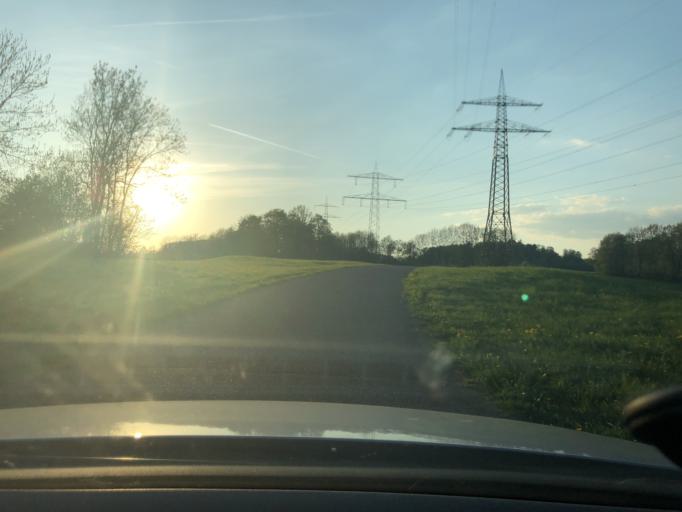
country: DE
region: Baden-Wuerttemberg
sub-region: Freiburg Region
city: Waldshut-Tiengen
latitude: 47.6460
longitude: 8.1957
